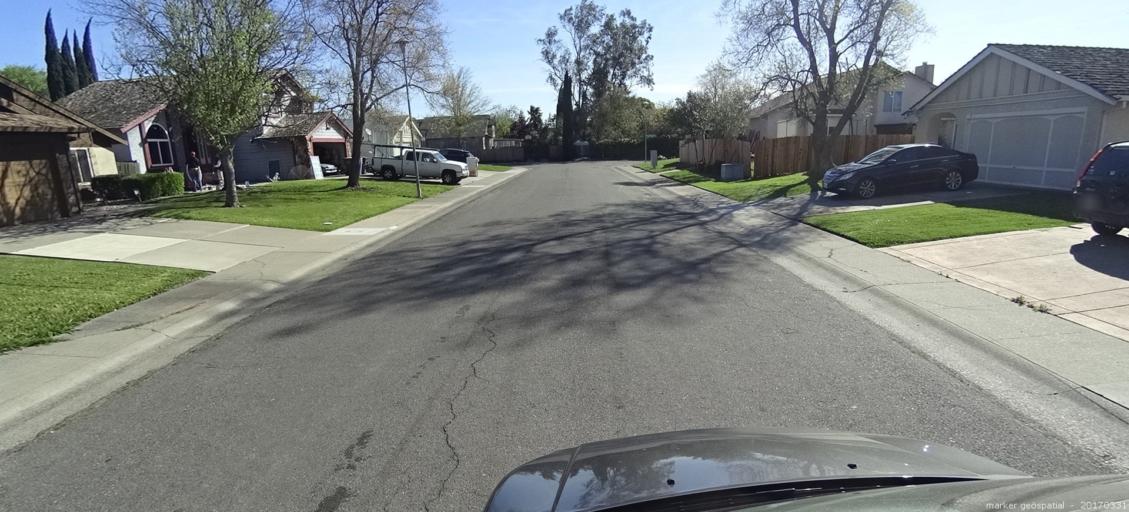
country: US
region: California
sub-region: Sacramento County
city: Parkway
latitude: 38.4663
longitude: -121.4608
